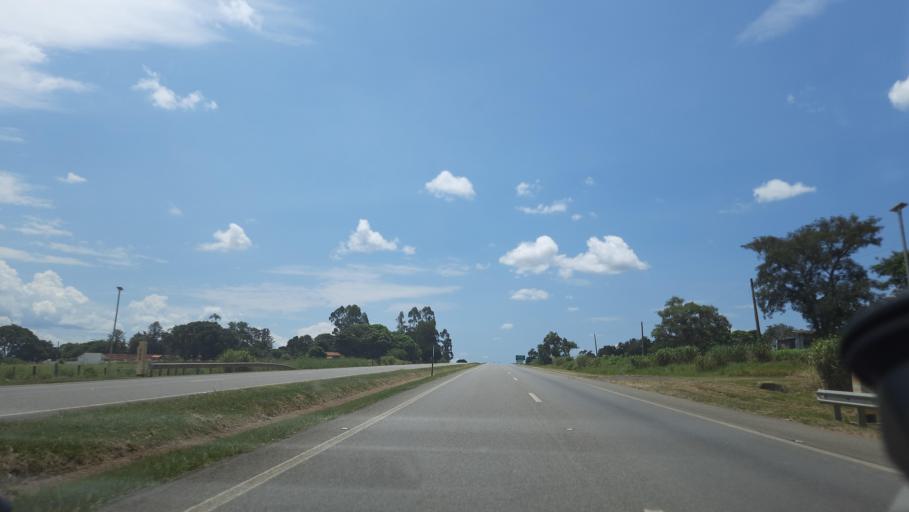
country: BR
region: Sao Paulo
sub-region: Mococa
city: Mococa
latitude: -21.5805
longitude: -47.0377
